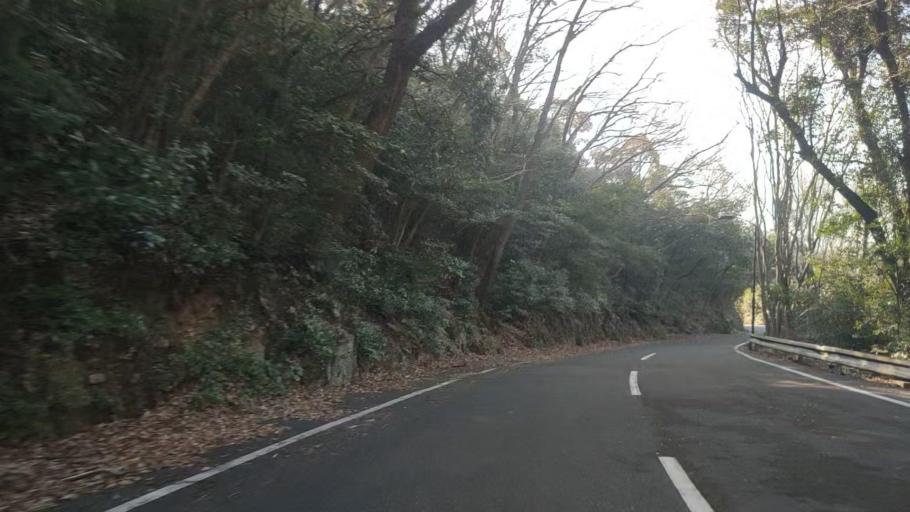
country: JP
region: Gifu
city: Gifu-shi
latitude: 35.4253
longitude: 136.7704
